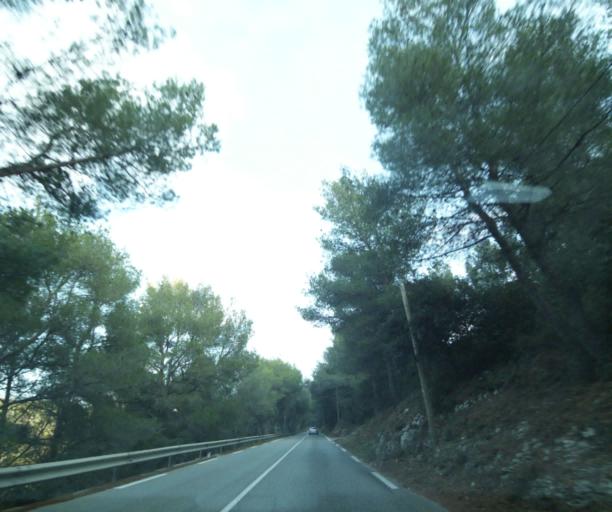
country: FR
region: Provence-Alpes-Cote d'Azur
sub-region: Departement des Bouches-du-Rhone
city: Cassis
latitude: 43.2226
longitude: 5.5736
